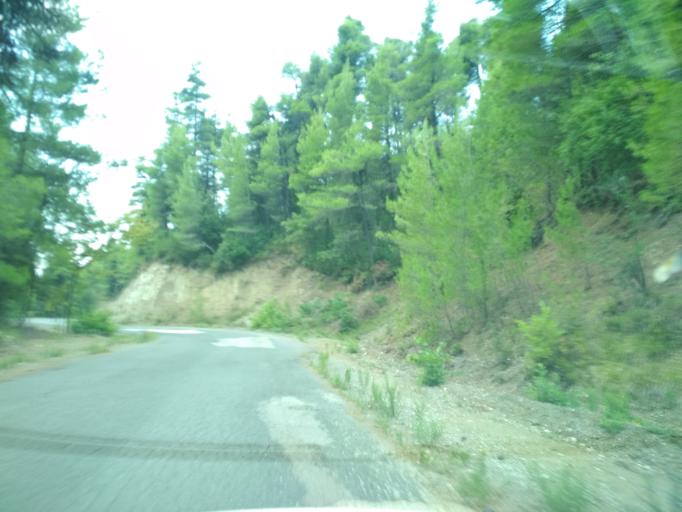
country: GR
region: Central Greece
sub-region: Nomos Evvoias
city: Roviai
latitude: 38.8507
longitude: 23.2823
